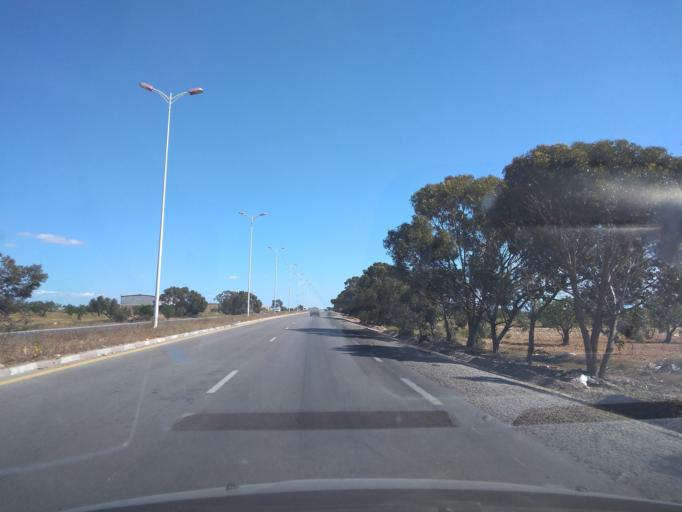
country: TN
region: Safaqis
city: Al Qarmadah
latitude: 34.8423
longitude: 10.7403
